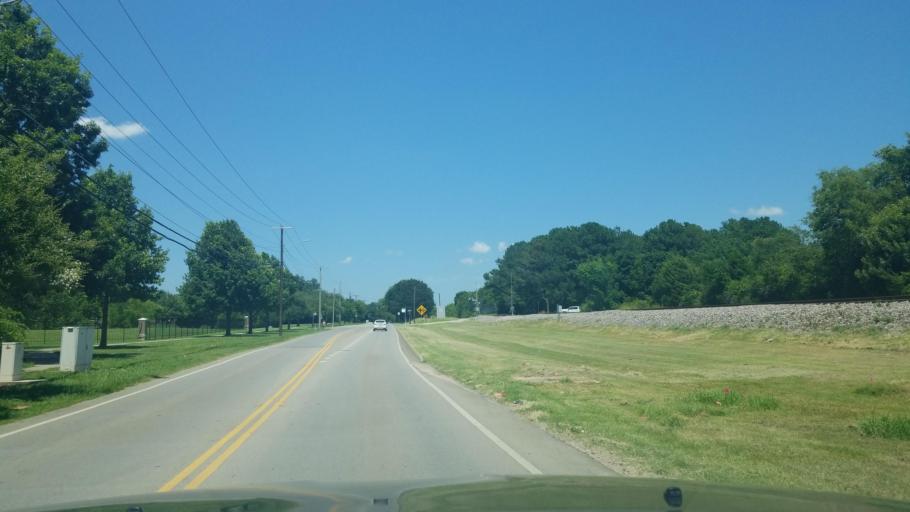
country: US
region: Texas
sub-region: Denton County
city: Denton
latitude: 33.2267
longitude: -97.1166
